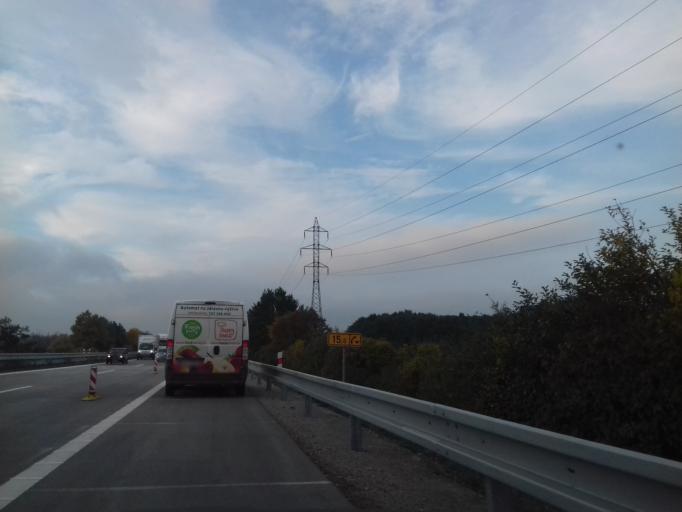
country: CZ
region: South Moravian
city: Nosislav
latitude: 49.0299
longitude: 16.6841
